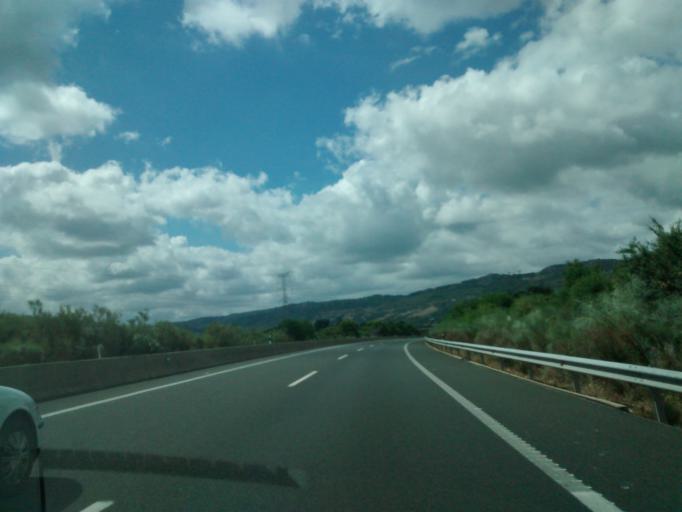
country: ES
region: Extremadura
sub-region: Provincia de Caceres
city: Casas de Miravete
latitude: 39.7423
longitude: -5.7251
